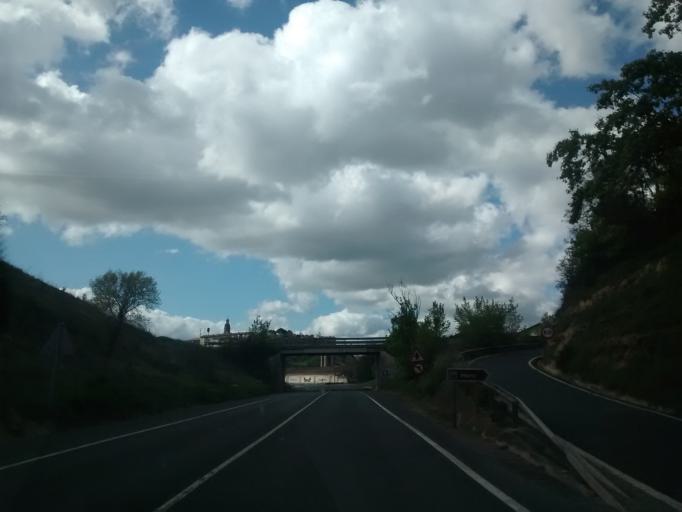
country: ES
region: La Rioja
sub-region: Provincia de La Rioja
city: Haro
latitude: 42.5864
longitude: -2.8451
